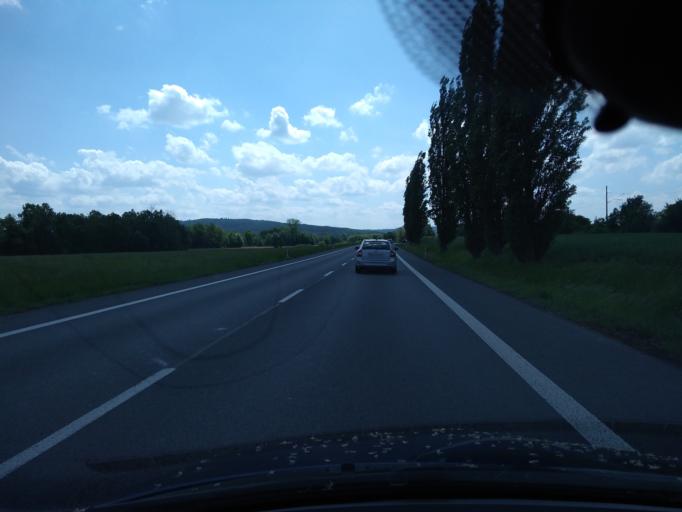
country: CZ
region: Plzensky
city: Svihov
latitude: 49.5217
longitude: 13.3005
